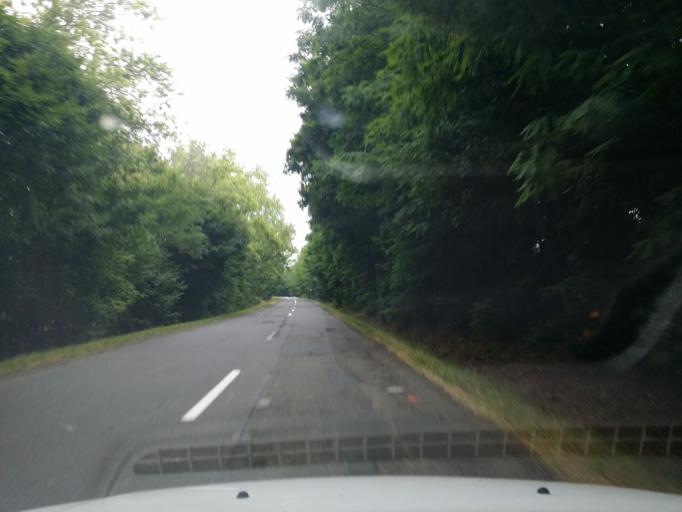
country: HU
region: Nograd
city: Bercel
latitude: 47.9478
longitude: 19.3597
